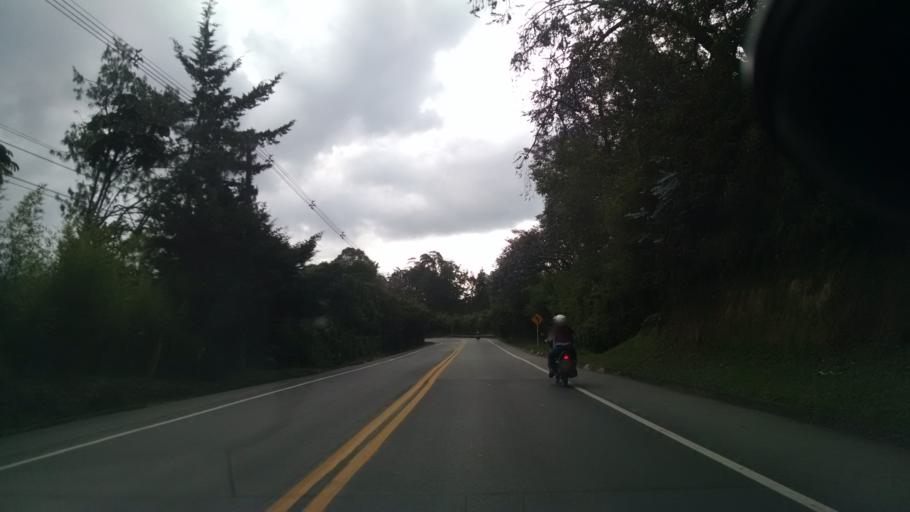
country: CO
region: Antioquia
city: El Retiro
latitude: 6.0923
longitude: -75.4948
